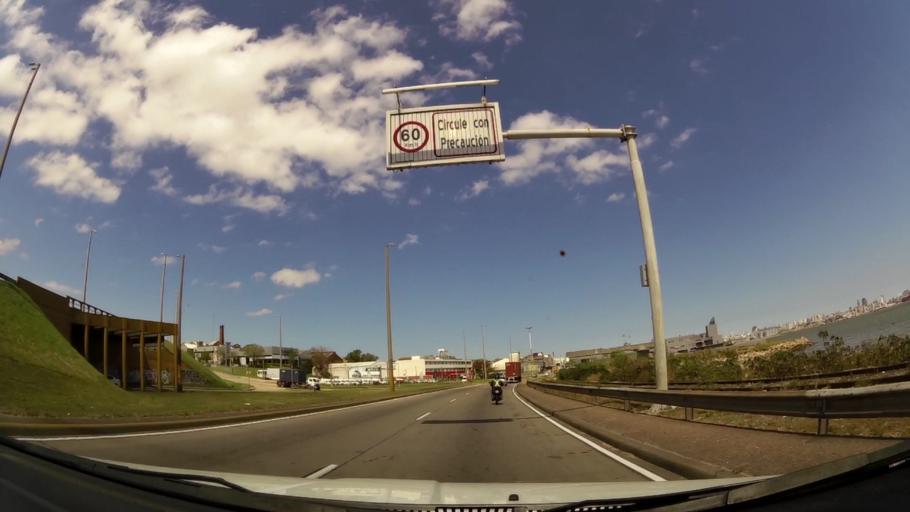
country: UY
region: Montevideo
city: Montevideo
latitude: -34.8751
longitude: -56.2117
